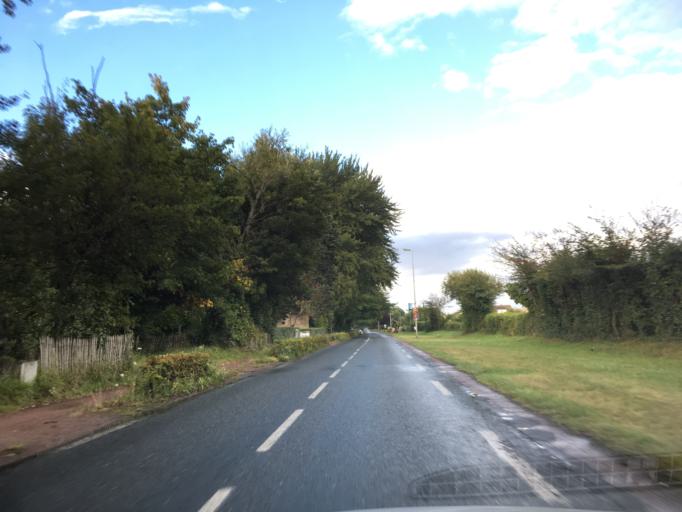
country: FR
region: Lower Normandy
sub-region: Departement du Calvados
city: Merville-Franceville-Plage
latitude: 49.2745
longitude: -0.2129
